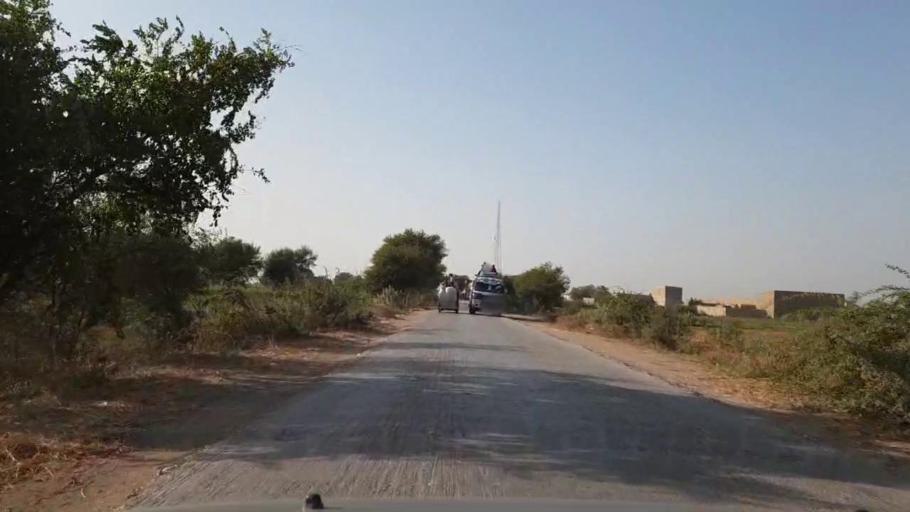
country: PK
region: Sindh
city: Chambar
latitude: 25.2104
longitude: 68.7815
